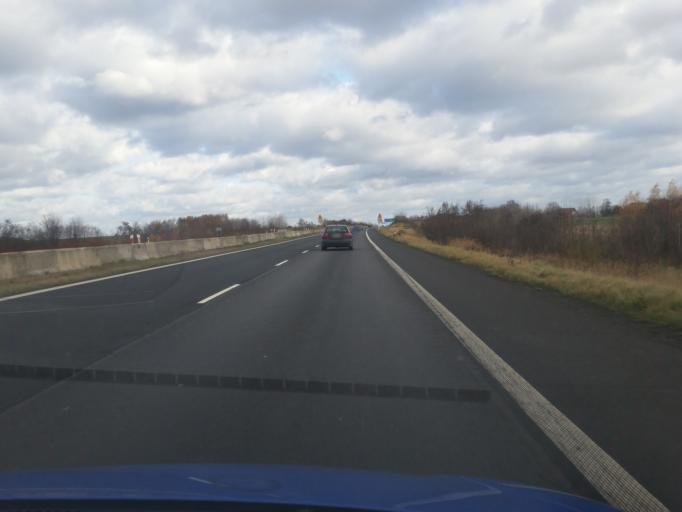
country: PL
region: Silesian Voivodeship
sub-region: Powiat czestochowski
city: Borowno
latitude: 50.9501
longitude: 19.2424
